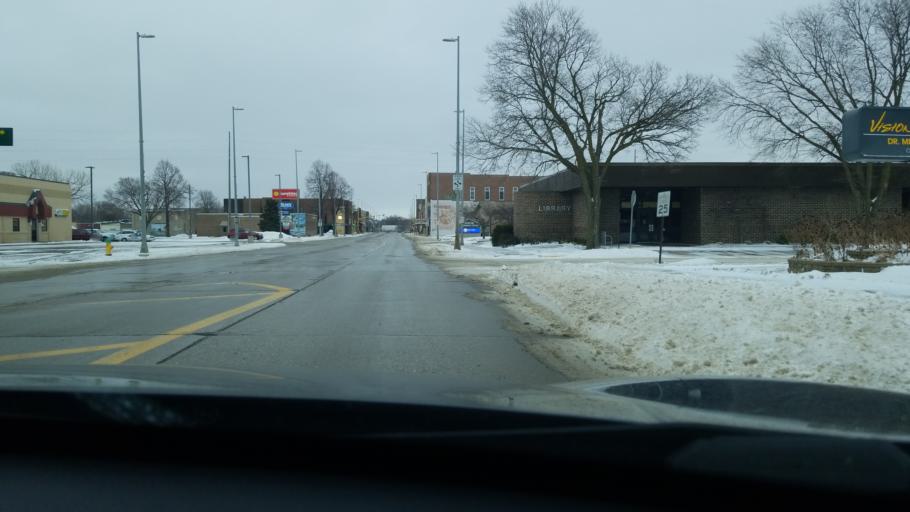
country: US
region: Iowa
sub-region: Lyon County
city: Rock Rapids
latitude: 43.4318
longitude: -96.1713
